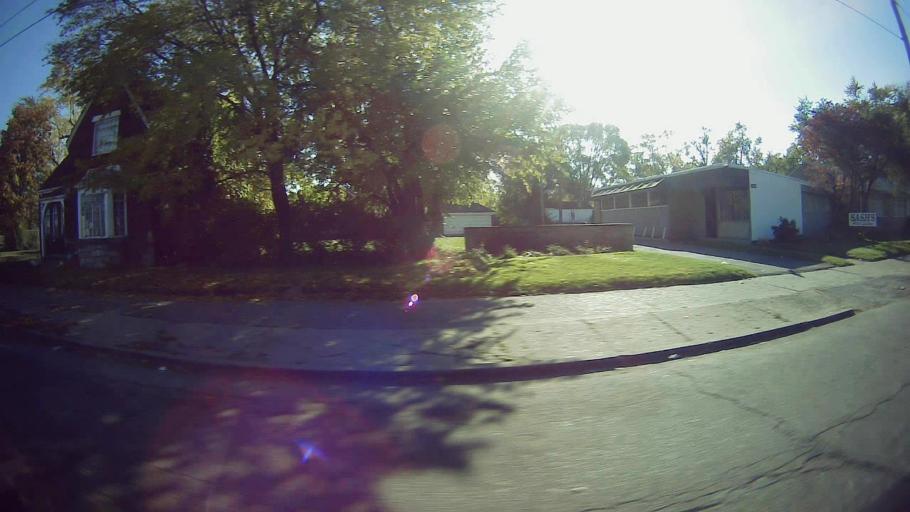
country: US
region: Michigan
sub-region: Oakland County
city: Ferndale
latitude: 42.4314
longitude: -83.1462
